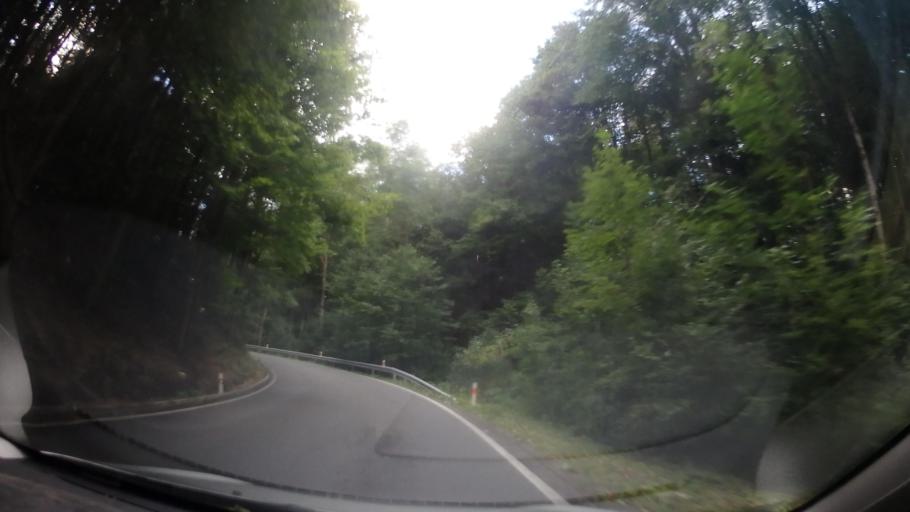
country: CZ
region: Olomoucky
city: Stity
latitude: 49.8802
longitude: 16.7840
